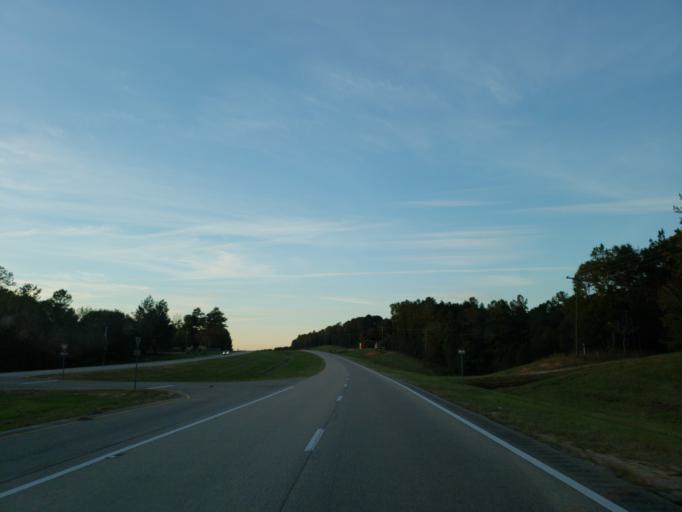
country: US
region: Mississippi
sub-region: Wayne County
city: Belmont
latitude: 31.4965
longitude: -88.4932
